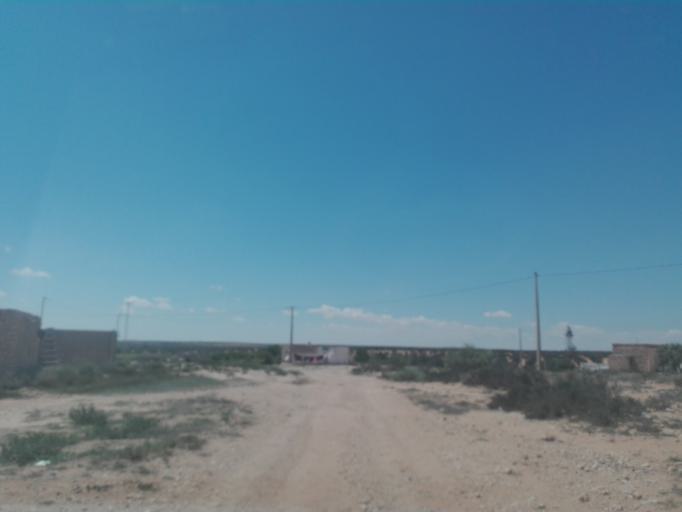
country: TN
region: Safaqis
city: Bi'r `Ali Bin Khalifah
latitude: 34.7861
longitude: 10.3349
